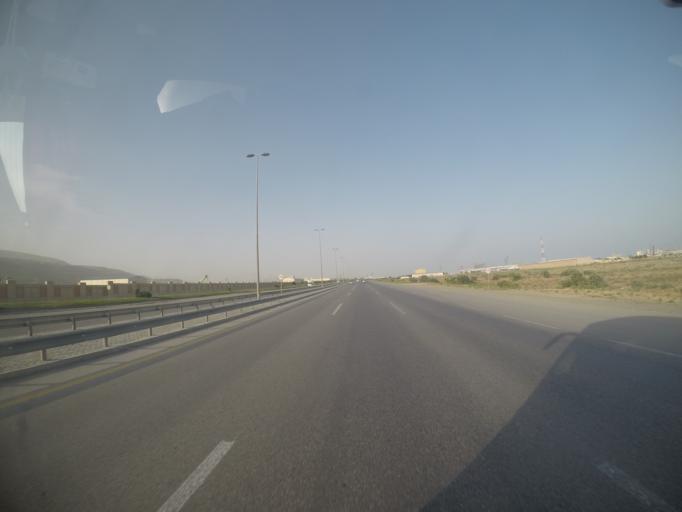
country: AZ
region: Baki
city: Puta
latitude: 40.2570
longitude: 49.6332
